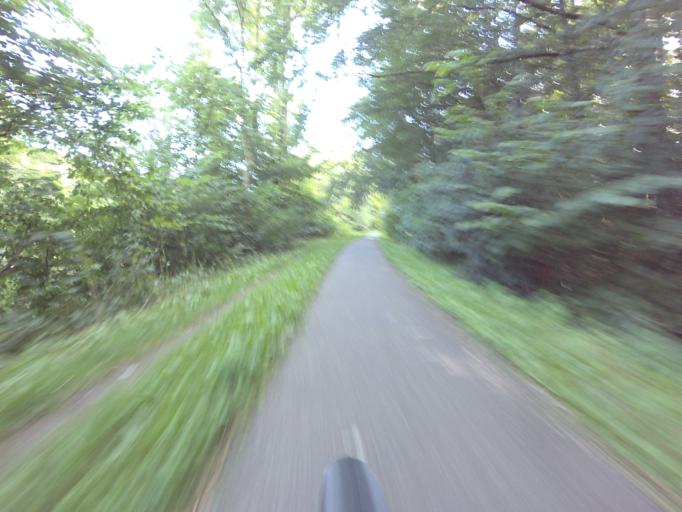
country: DK
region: Central Jutland
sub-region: Horsens Kommune
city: Horsens
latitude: 55.9297
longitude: 9.7683
